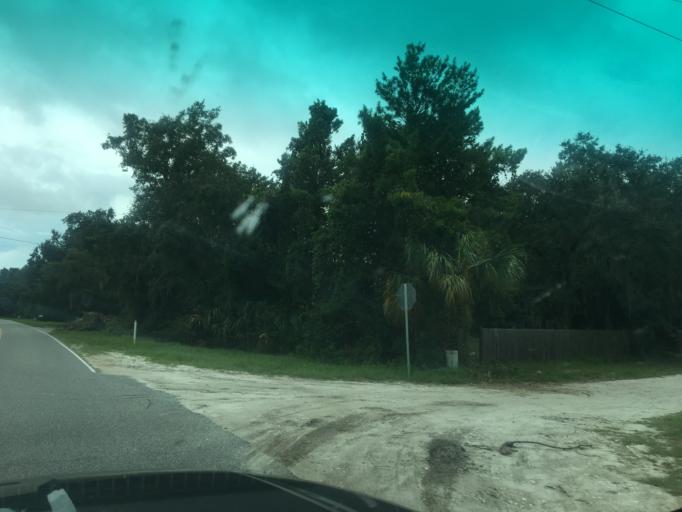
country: US
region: Florida
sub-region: Wakulla County
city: Crawfordville
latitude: 29.9134
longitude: -84.3667
